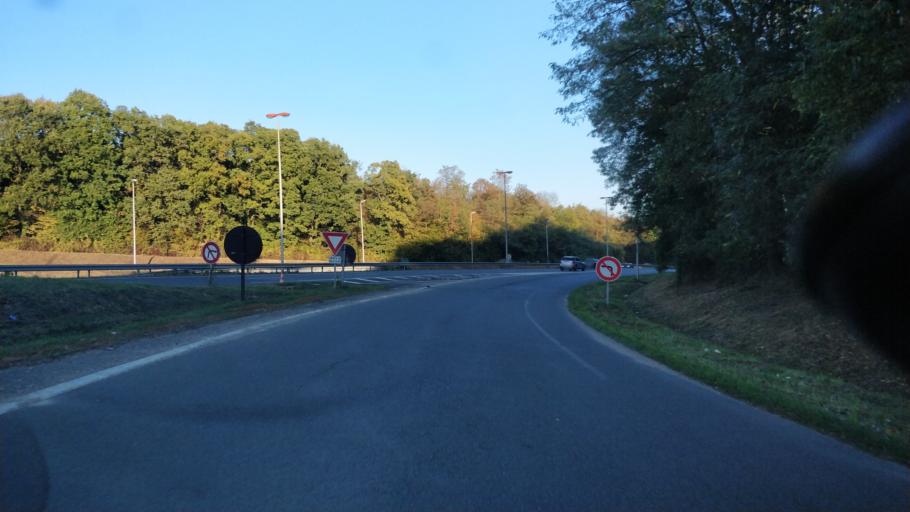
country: FR
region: Ile-de-France
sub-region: Departement de Seine-et-Marne
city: Champs-sur-Marne
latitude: 48.8489
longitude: 2.5883
